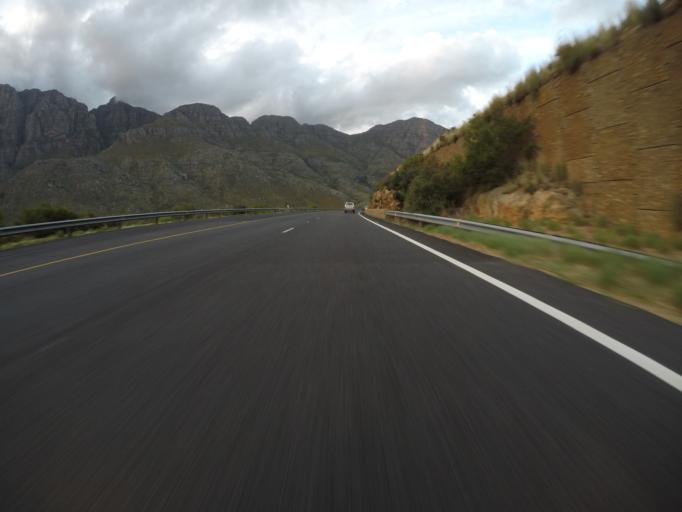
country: ZA
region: Western Cape
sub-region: Cape Winelands District Municipality
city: Paarl
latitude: -33.7032
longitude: 19.2035
